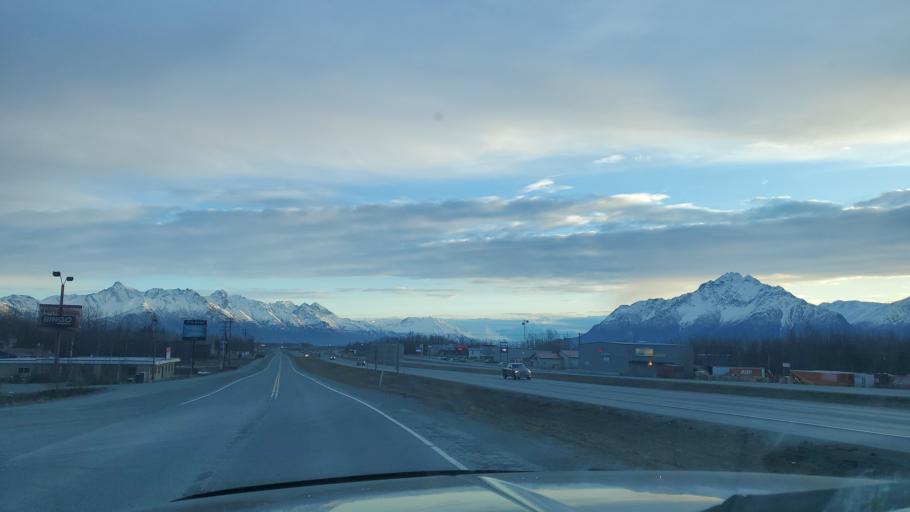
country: US
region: Alaska
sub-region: Matanuska-Susitna Borough
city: Lakes
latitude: 61.5632
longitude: -149.2960
